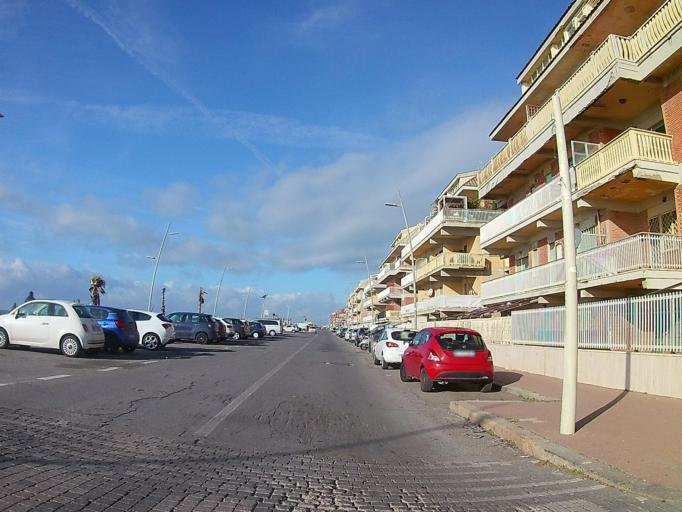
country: IT
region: Latium
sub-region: Citta metropolitana di Roma Capitale
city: Lido di Ostia
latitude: 41.7348
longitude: 12.2609
